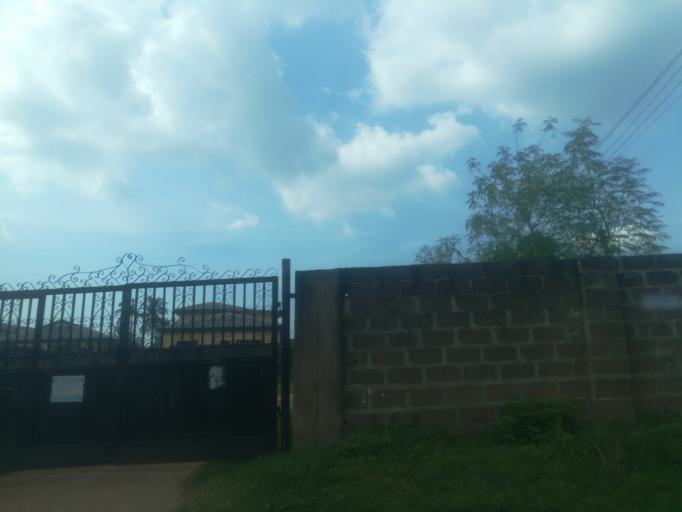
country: NG
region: Ogun
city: Abeokuta
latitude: 7.1174
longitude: 3.3296
